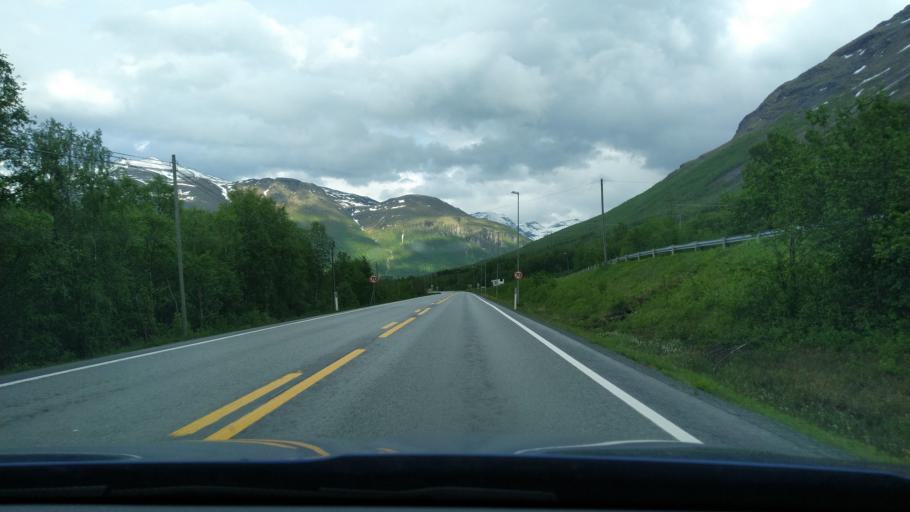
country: NO
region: Troms
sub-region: Balsfjord
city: Storsteinnes
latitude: 69.2135
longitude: 19.5265
